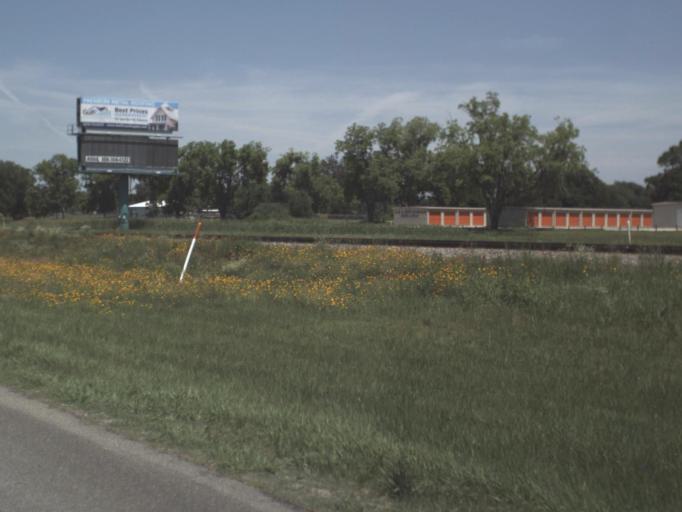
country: US
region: Florida
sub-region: Suwannee County
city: Live Oak
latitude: 30.2850
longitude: -82.9570
